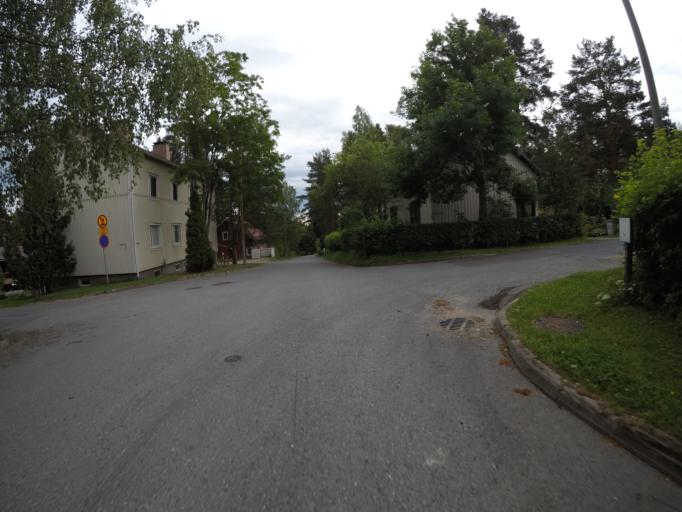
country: FI
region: Haeme
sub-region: Haemeenlinna
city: Haemeenlinna
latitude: 60.9844
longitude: 24.4542
